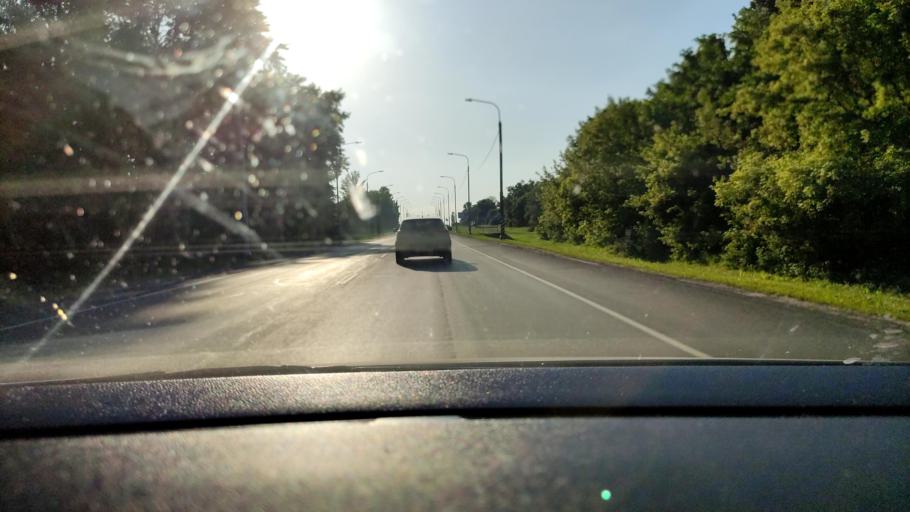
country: RU
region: Voronezj
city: Kashirskoye
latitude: 51.4973
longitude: 39.5915
